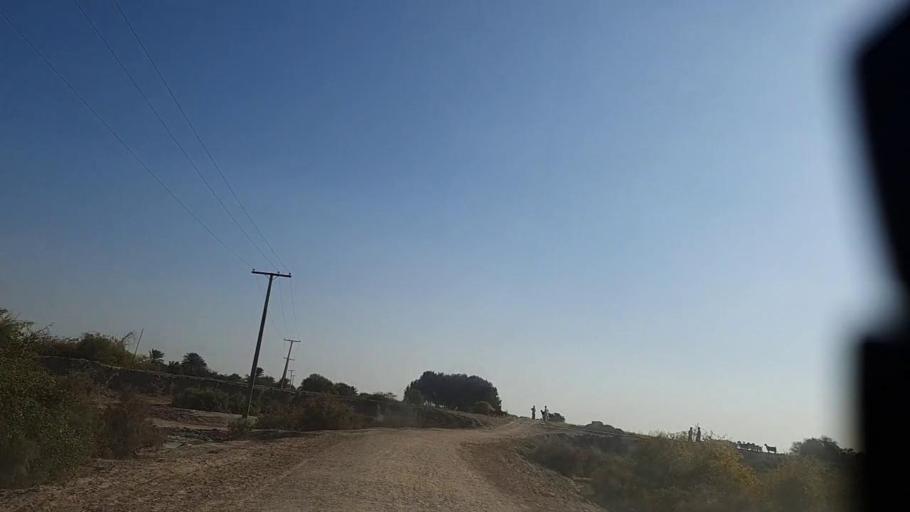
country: PK
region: Sindh
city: Digri
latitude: 25.1476
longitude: 69.0373
